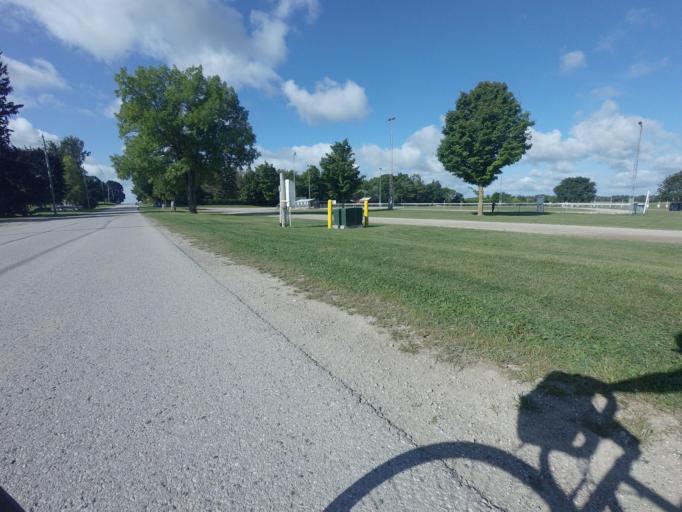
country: CA
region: Ontario
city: Huron East
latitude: 43.7348
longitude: -81.4329
